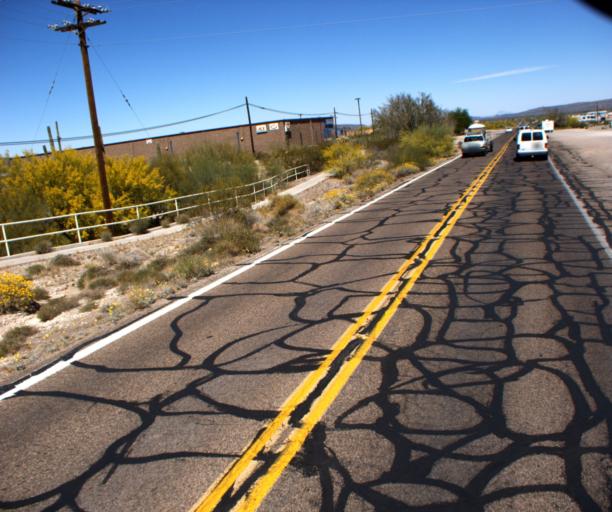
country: US
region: Arizona
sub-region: Pima County
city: Ajo
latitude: 32.3911
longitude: -112.8722
